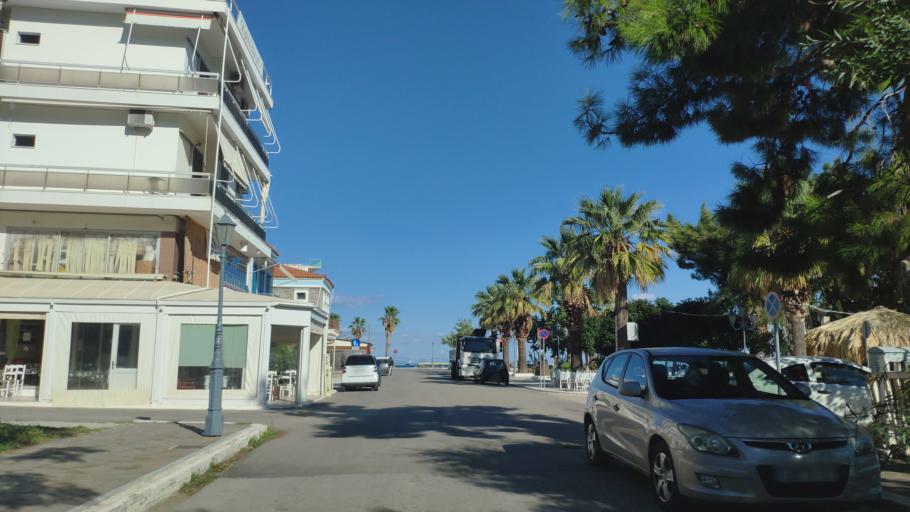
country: GR
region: Attica
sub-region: Nomos Piraios
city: Galatas
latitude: 37.5786
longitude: 23.3888
